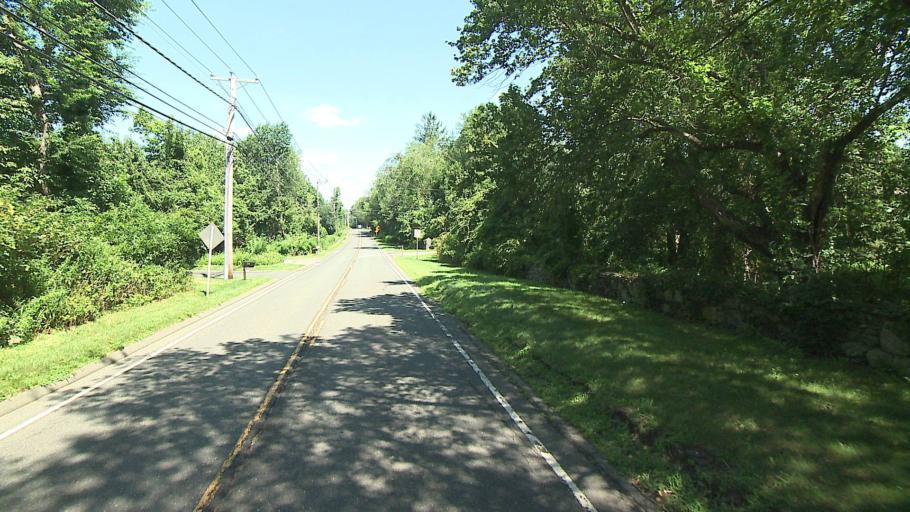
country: US
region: Connecticut
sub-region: New Haven County
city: Oxford
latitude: 41.3728
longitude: -73.1923
